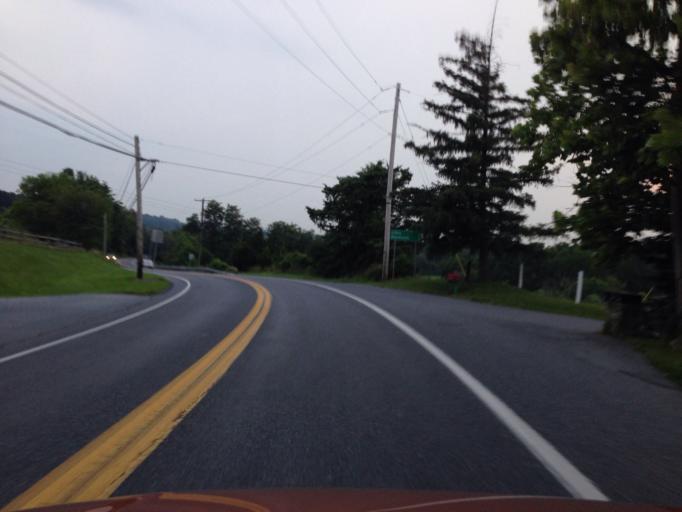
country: US
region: Pennsylvania
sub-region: Lancaster County
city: Rothsville
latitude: 40.1510
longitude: -76.2636
